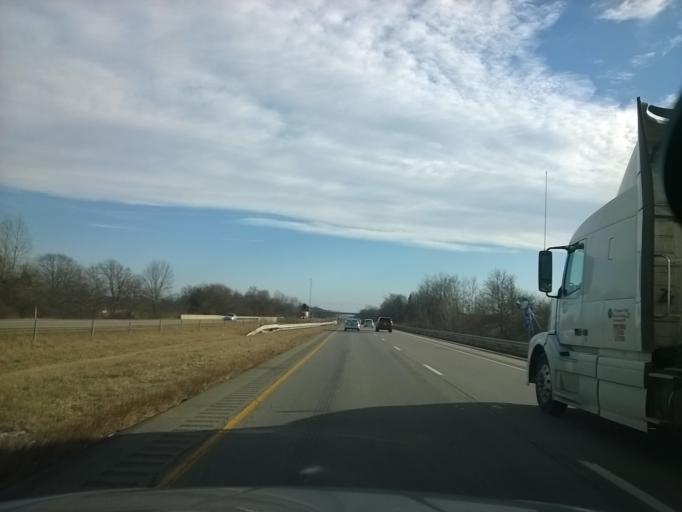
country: US
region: Indiana
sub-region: Johnson County
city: Franklin
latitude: 39.4465
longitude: -85.9919
